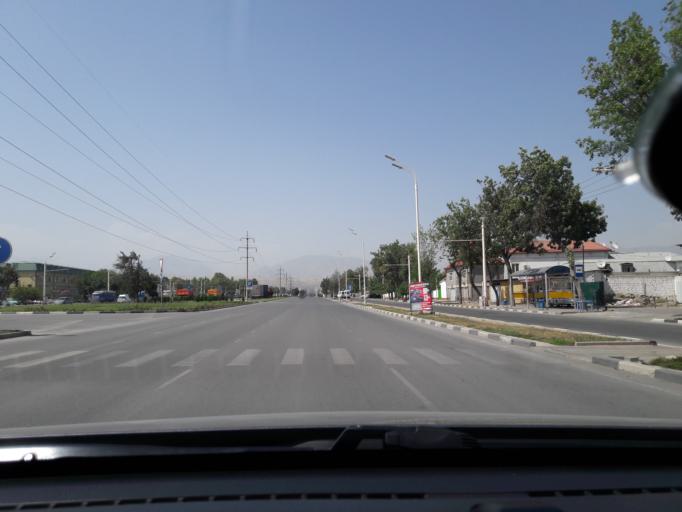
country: TJ
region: Dushanbe
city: Dushanbe
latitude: 38.5397
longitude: 68.7414
